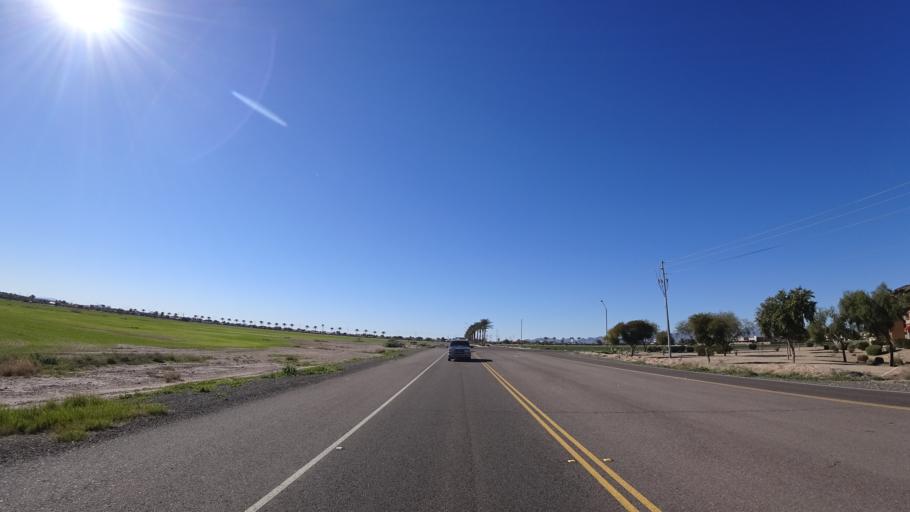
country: US
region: Arizona
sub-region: Maricopa County
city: Goodyear
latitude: 33.4355
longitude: -112.3873
